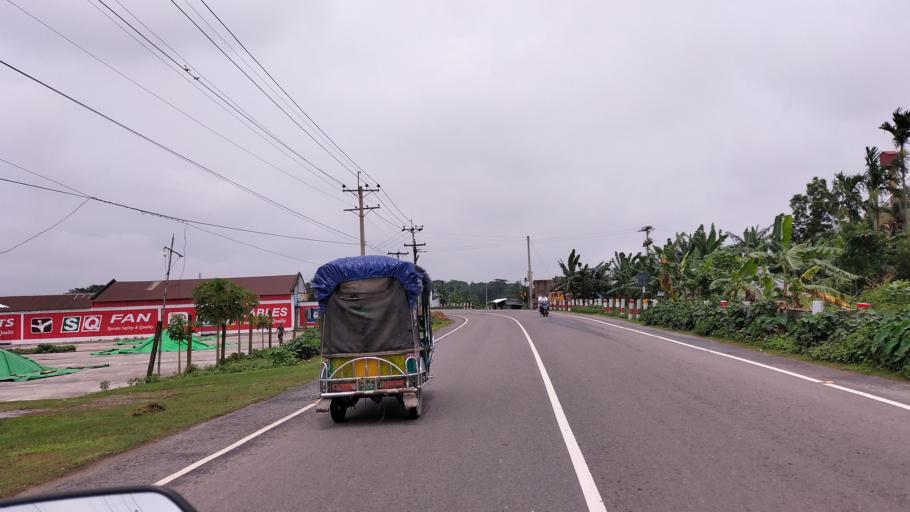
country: BD
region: Dhaka
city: Netrakona
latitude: 24.8523
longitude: 90.6541
